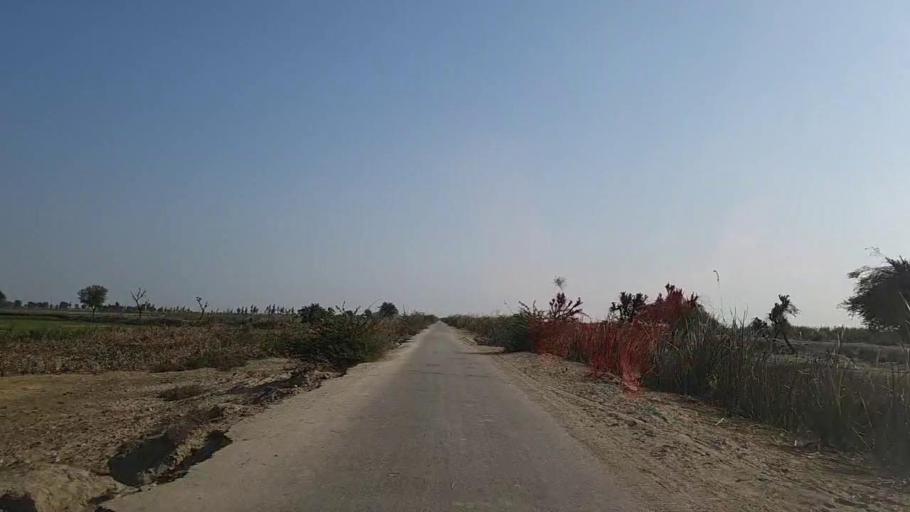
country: PK
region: Sindh
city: Sanghar
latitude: 25.9423
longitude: 69.0534
